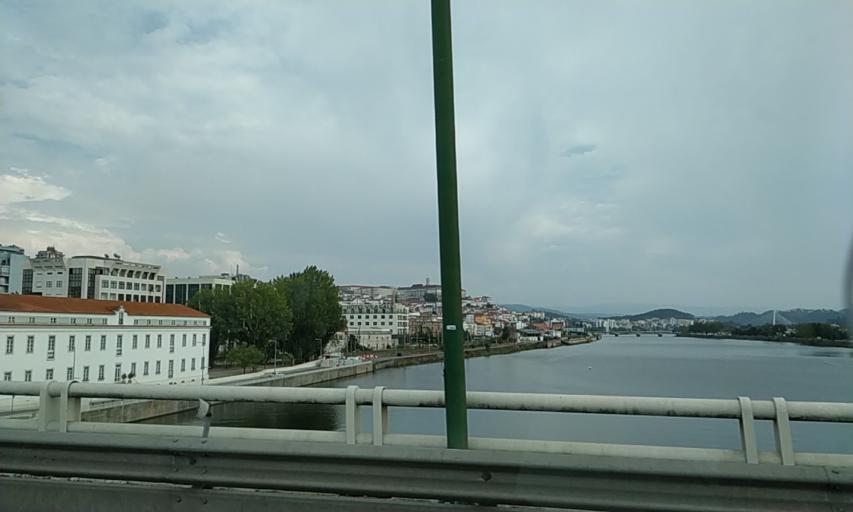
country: PT
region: Coimbra
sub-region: Coimbra
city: Coimbra
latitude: 40.2156
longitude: -8.4399
